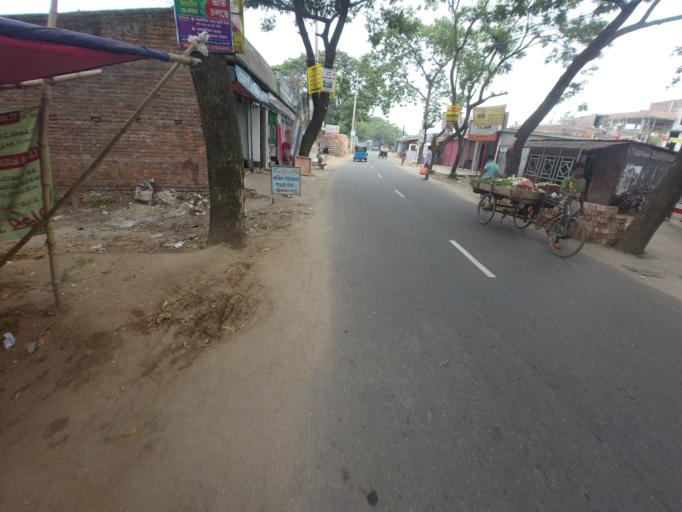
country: BD
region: Dhaka
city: Azimpur
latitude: 23.7274
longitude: 90.3402
